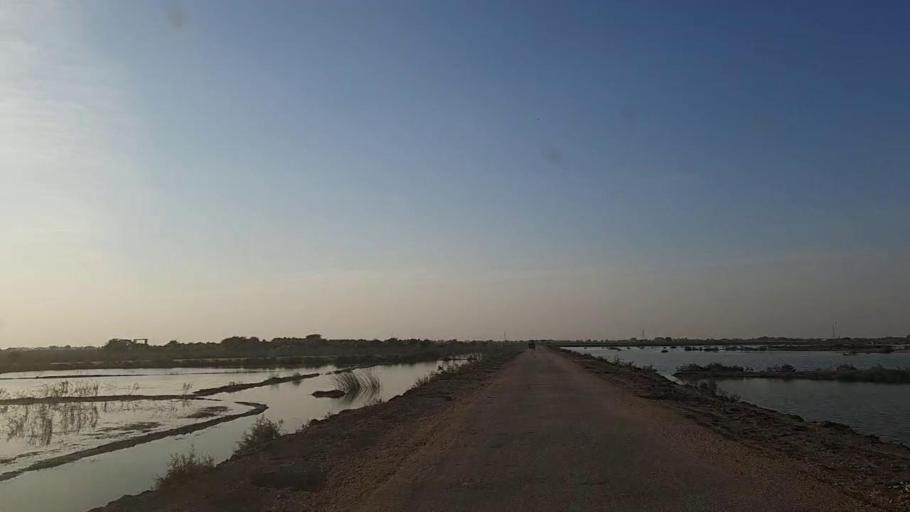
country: PK
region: Sindh
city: Mirpur Batoro
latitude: 24.6852
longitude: 68.2070
